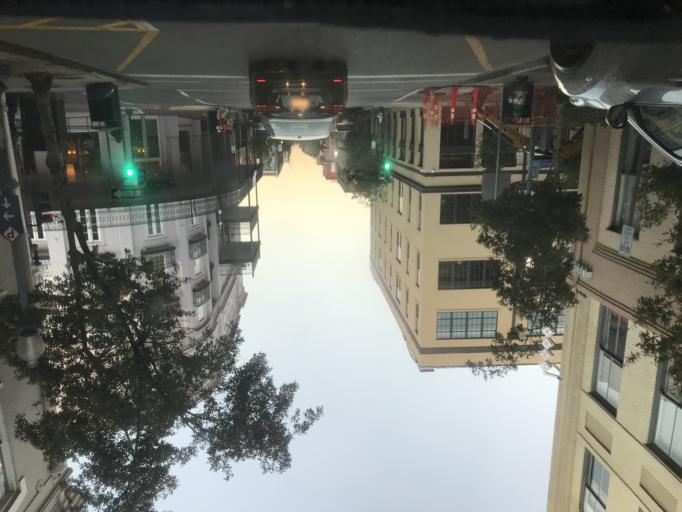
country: US
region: Louisiana
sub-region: Orleans Parish
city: New Orleans
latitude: 29.9469
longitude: -90.0690
